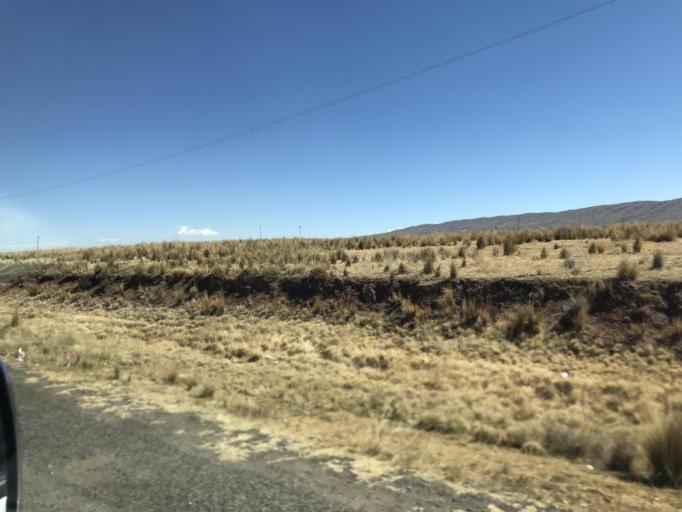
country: BO
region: La Paz
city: Tiahuanaco
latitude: -16.5704
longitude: -68.6690
